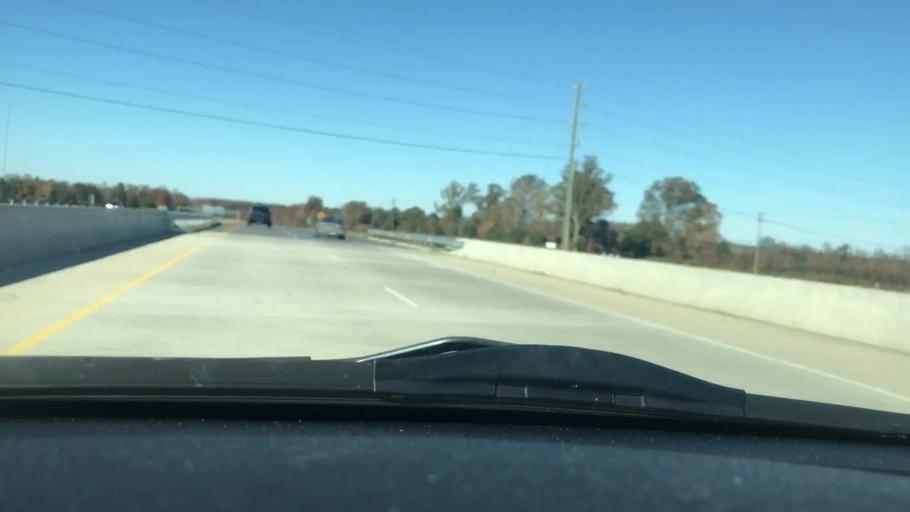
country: US
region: North Carolina
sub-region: Guilford County
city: Summerfield
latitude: 36.2469
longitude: -79.9210
